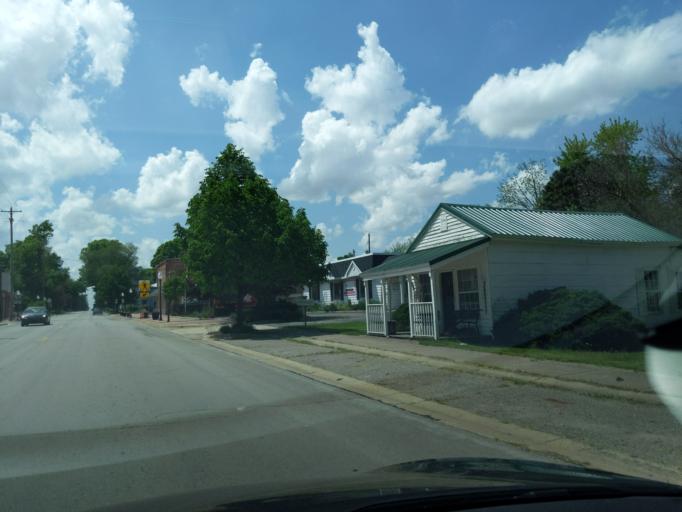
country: US
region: Michigan
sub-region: Ingham County
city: Williamston
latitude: 42.5559
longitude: -84.3021
